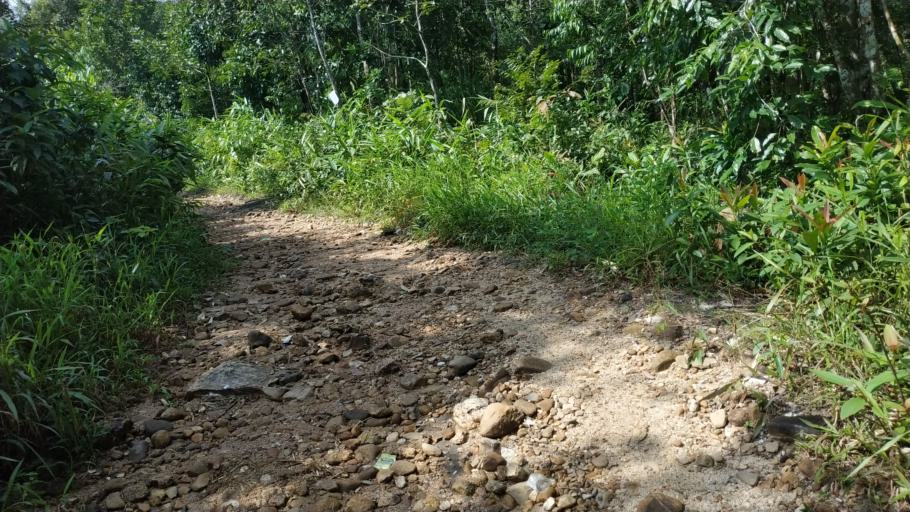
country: MM
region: Tanintharyi
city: Dawei
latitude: 14.5853
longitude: 98.0494
